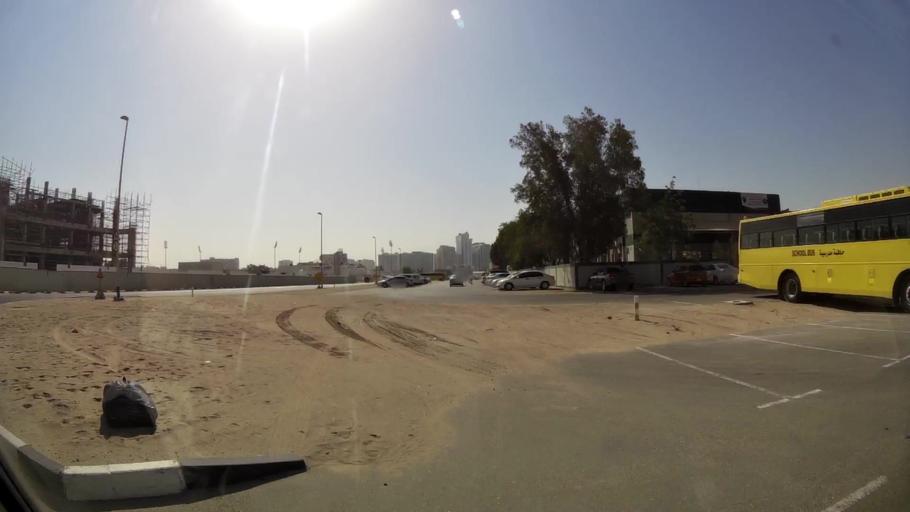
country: AE
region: Ash Shariqah
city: Sharjah
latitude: 25.2806
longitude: 55.3676
